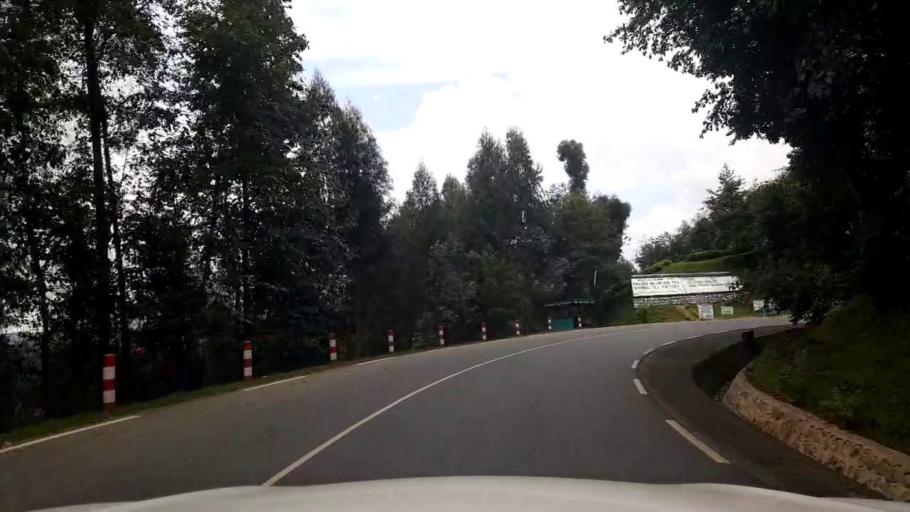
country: RW
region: Northern Province
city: Musanze
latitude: -1.6582
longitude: 29.5118
